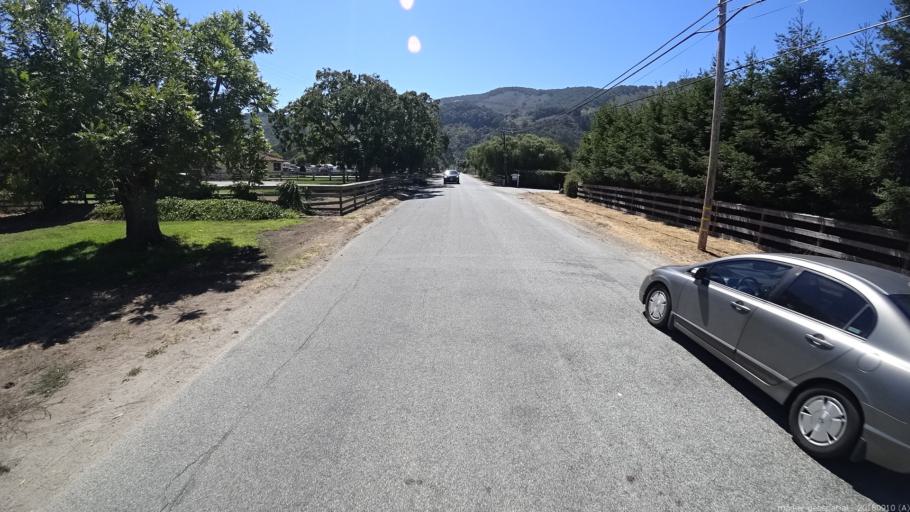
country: US
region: California
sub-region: Monterey County
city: Del Rey Oaks
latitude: 36.5288
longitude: -121.8307
